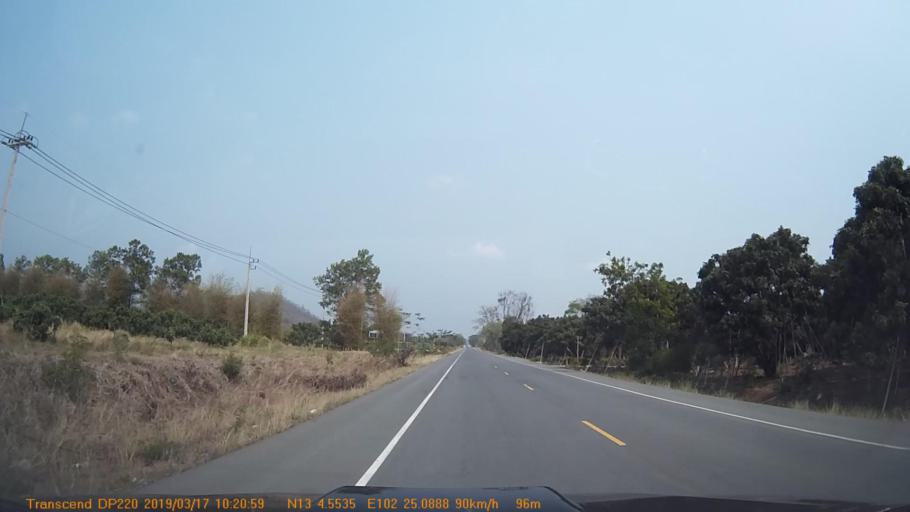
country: TH
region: Chanthaburi
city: Soi Dao
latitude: 13.0762
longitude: 102.4180
